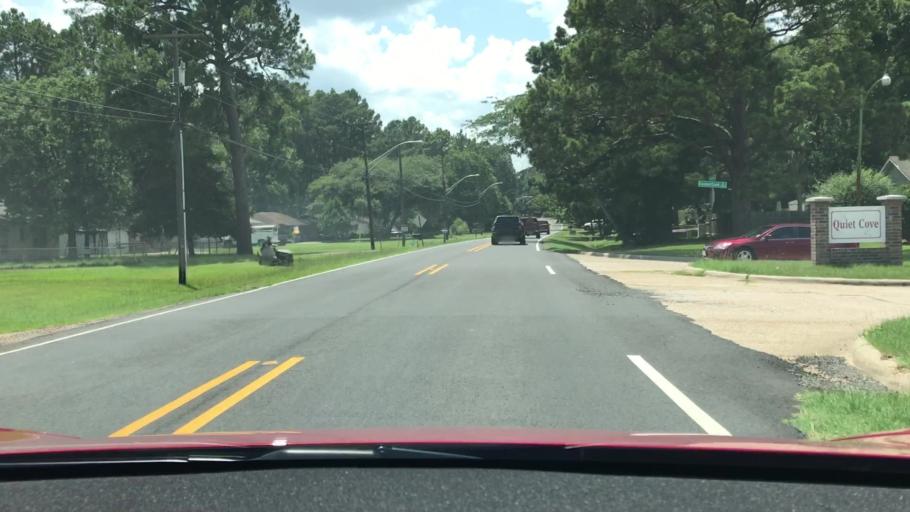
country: US
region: Louisiana
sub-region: De Soto Parish
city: Stonewall
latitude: 32.3910
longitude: -93.7713
